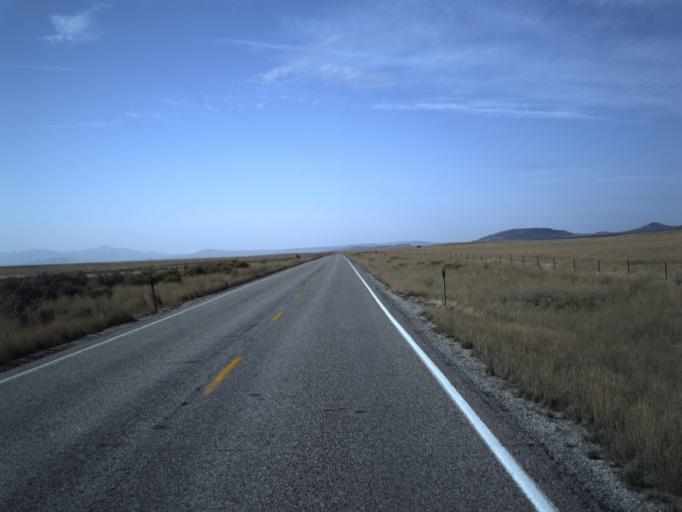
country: US
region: Idaho
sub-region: Oneida County
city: Malad City
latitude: 41.9316
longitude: -113.0892
